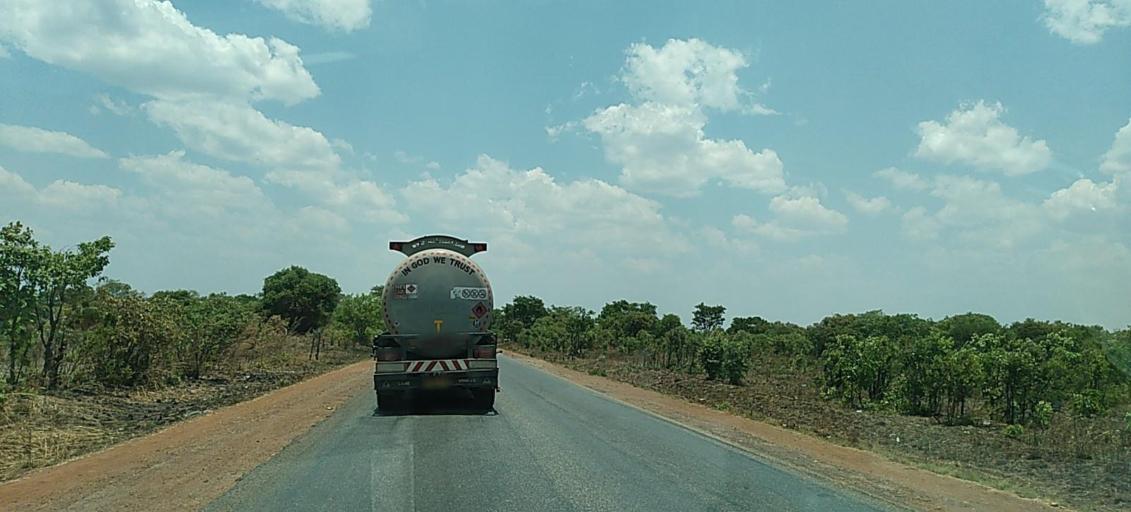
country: ZM
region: Central
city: Kapiri Mposhi
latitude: -13.7794
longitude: 28.6456
